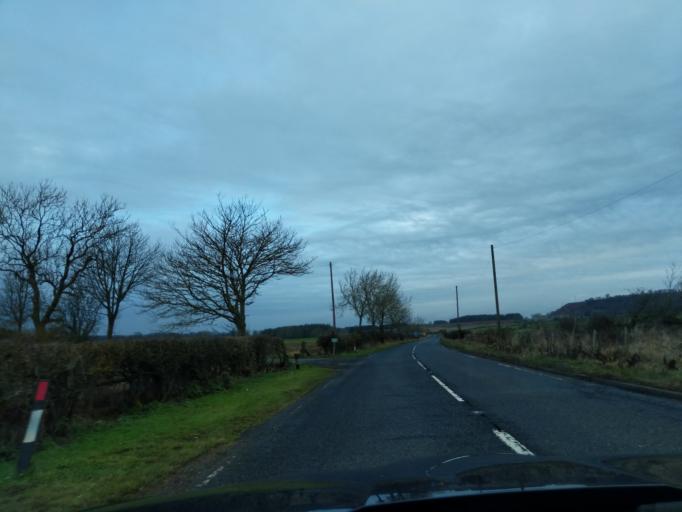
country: GB
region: England
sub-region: Northumberland
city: Rothley
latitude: 55.1191
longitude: -1.9088
